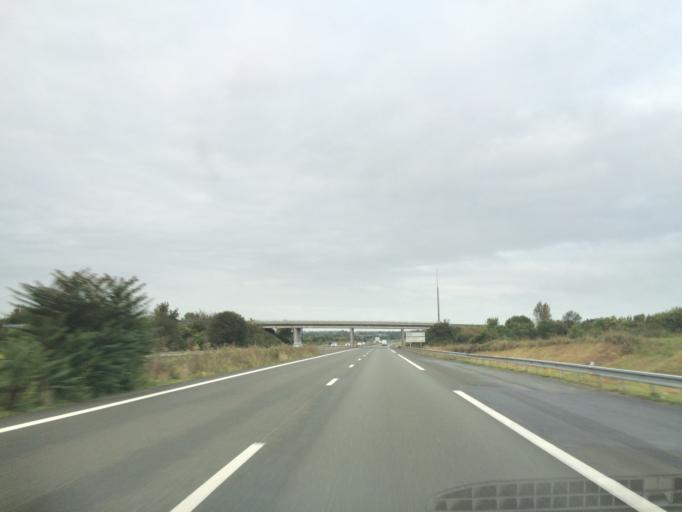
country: FR
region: Pays de la Loire
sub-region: Departement de Maine-et-Loire
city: Saint-Leger-des-Bois
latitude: 47.4589
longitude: -0.7004
